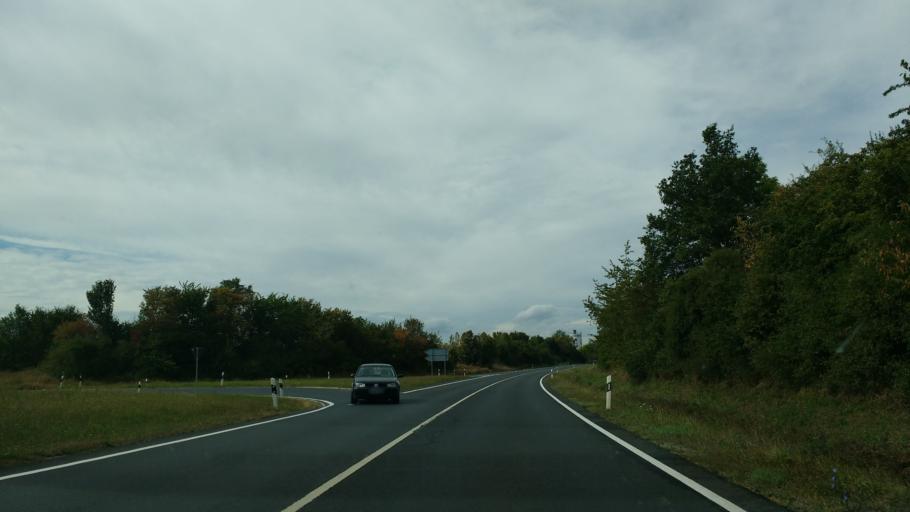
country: DE
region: Bavaria
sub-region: Regierungsbezirk Unterfranken
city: Gerolzhofen
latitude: 49.9059
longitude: 10.3528
